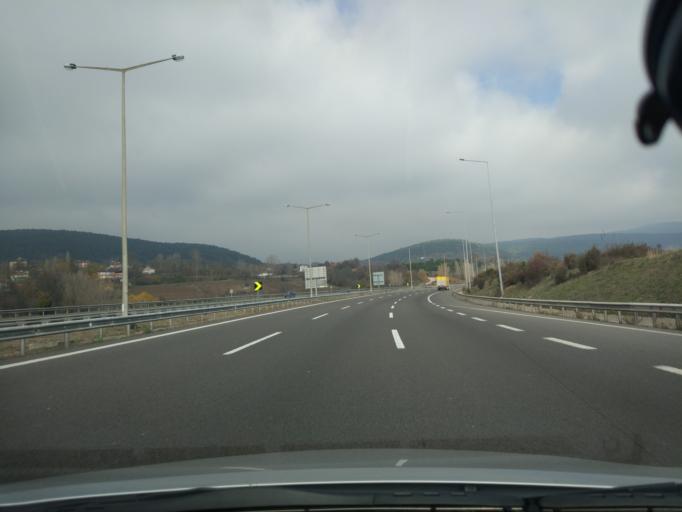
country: TR
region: Bolu
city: Bolu
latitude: 40.7469
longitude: 31.5614
